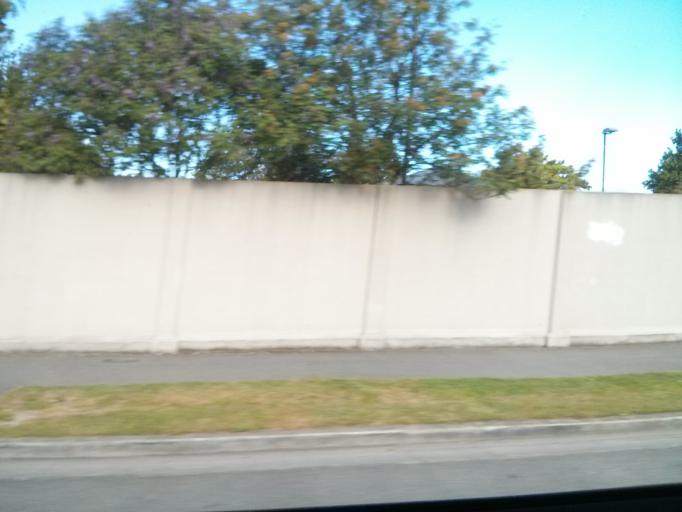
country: NZ
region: Canterbury
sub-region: Christchurch City
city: Christchurch
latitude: -43.5201
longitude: 172.5901
